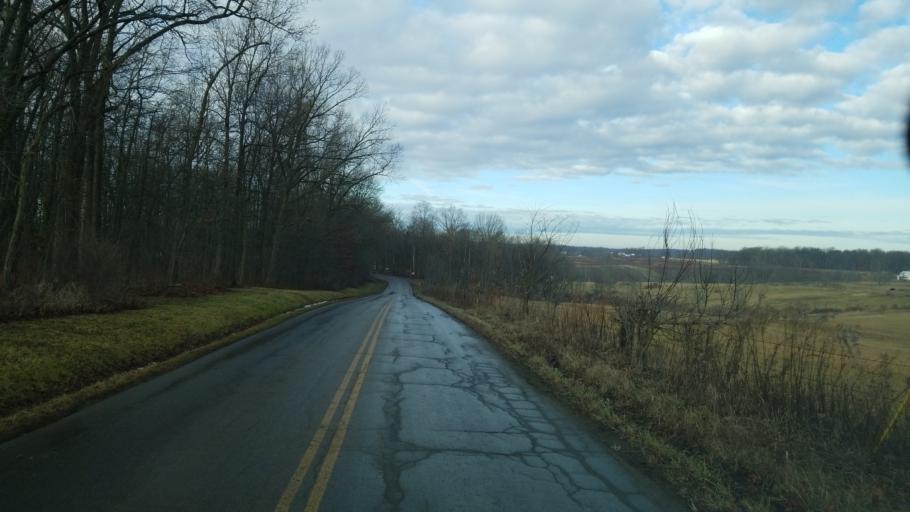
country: US
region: Ohio
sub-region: Knox County
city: Oak Hill
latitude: 40.3123
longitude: -82.2805
